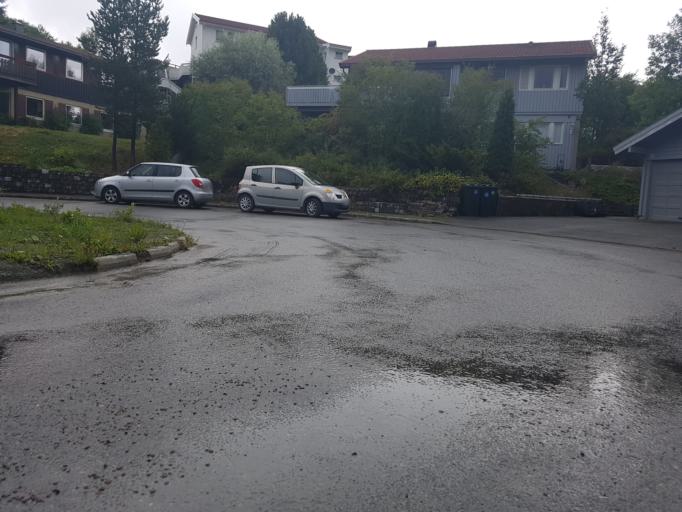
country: NO
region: Sor-Trondelag
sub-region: Trondheim
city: Trondheim
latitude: 63.3888
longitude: 10.3550
